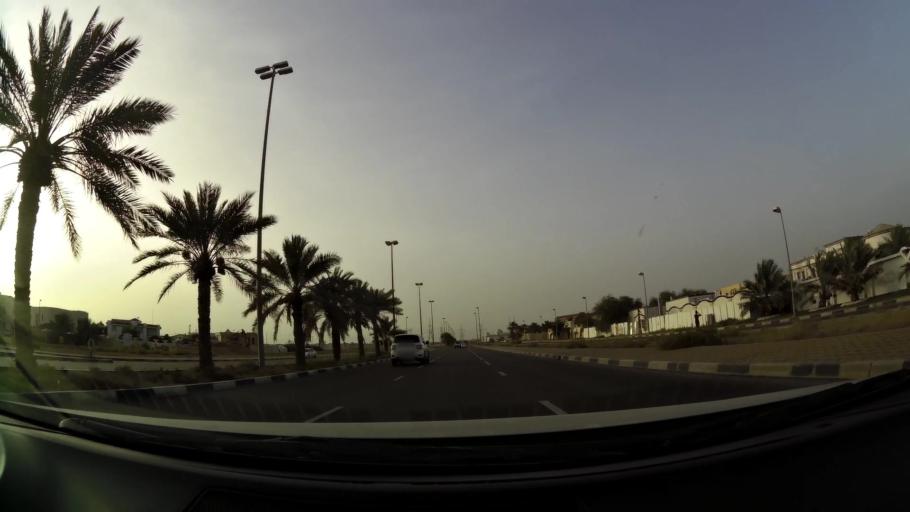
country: OM
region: Al Buraimi
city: Al Buraymi
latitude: 24.2668
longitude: 55.7205
